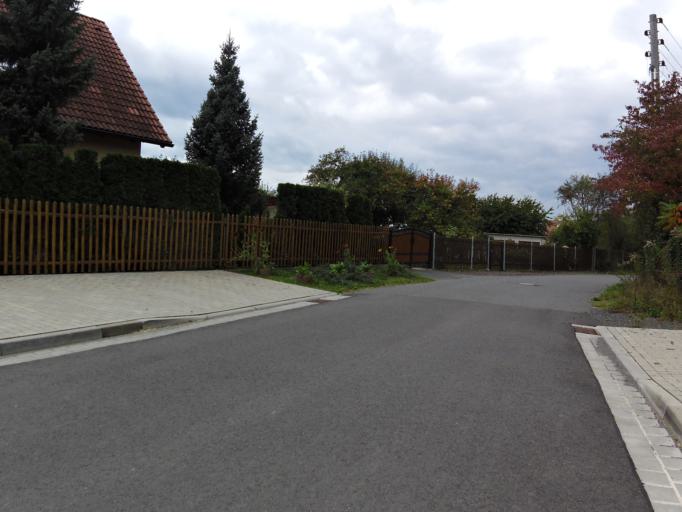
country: DE
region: Saxony
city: Grossposna
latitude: 51.3137
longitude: 12.4704
